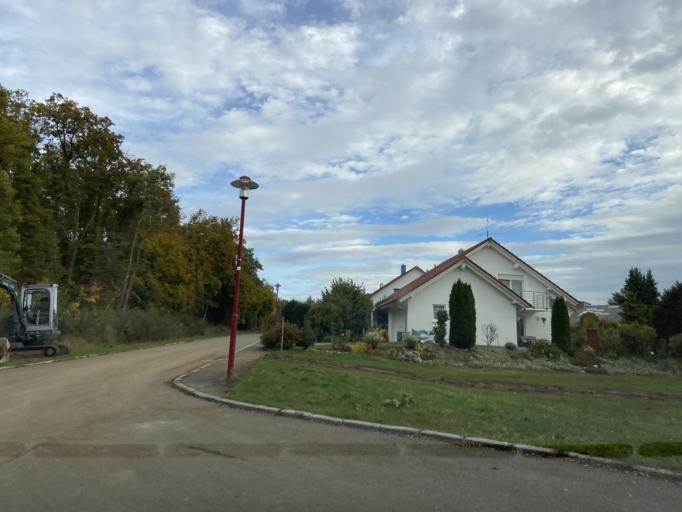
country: DE
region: Baden-Wuerttemberg
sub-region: Tuebingen Region
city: Bingen
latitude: 48.1131
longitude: 9.2635
